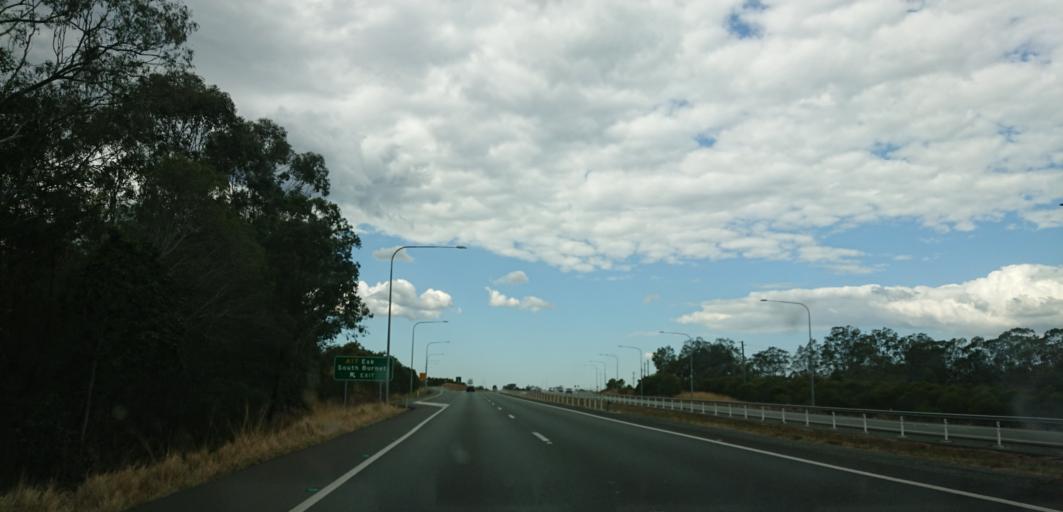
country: AU
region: Queensland
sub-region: Ipswich
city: Brassall
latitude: -27.5769
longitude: 152.6940
